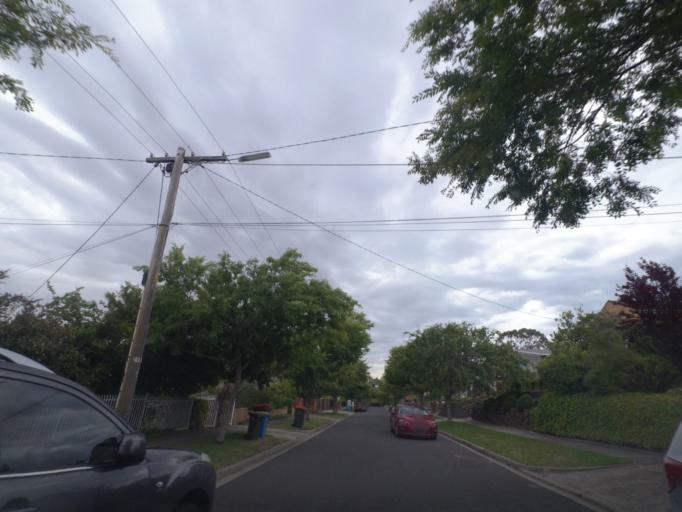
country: AU
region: Victoria
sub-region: Boroondara
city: Balwyn North
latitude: -37.7891
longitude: 145.0948
